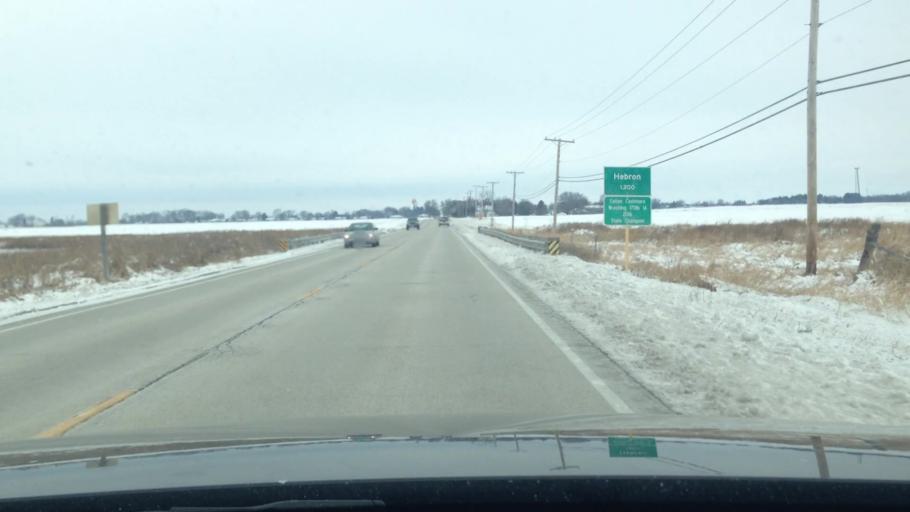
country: US
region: Illinois
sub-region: McHenry County
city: Hebron
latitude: 42.4503
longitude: -88.4330
